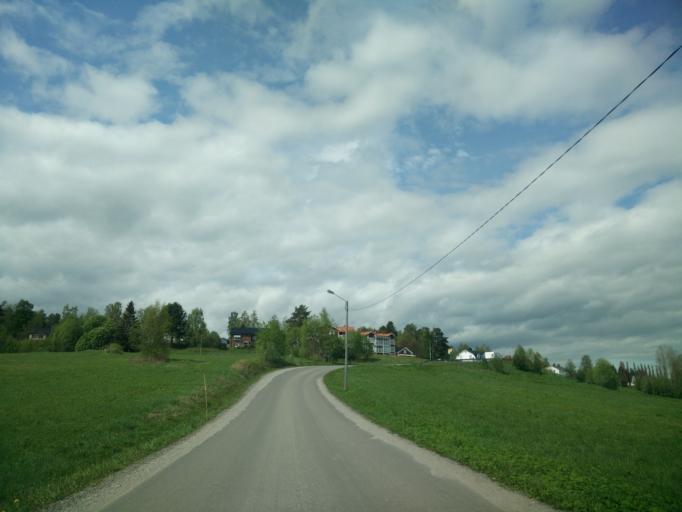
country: SE
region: Vaesternorrland
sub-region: Sundsvalls Kommun
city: Sundsvall
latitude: 62.3683
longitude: 17.2680
